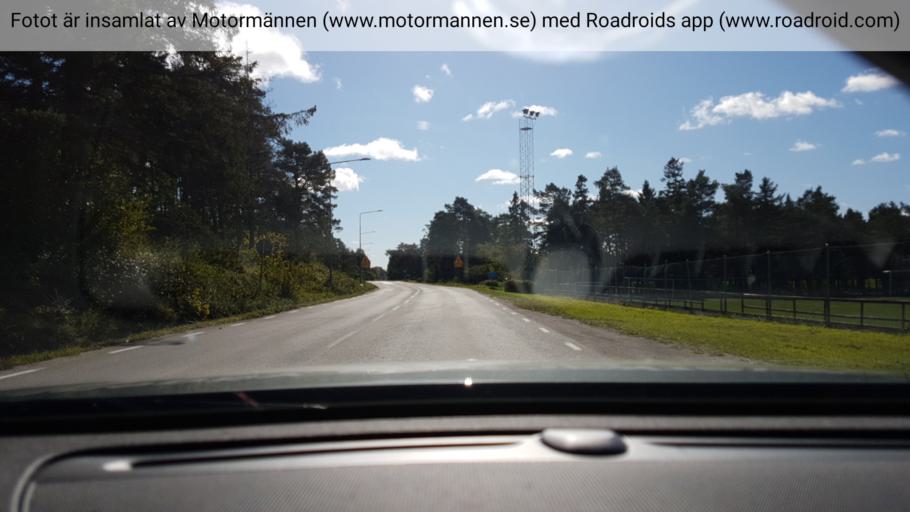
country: SE
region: Gotland
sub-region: Gotland
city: Slite
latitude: 57.7081
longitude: 18.7941
